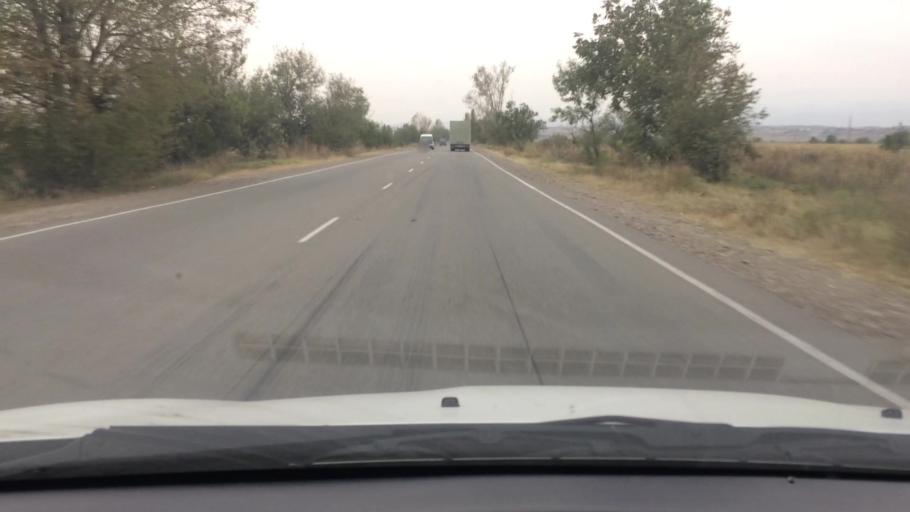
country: GE
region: Kvemo Kartli
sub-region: Marneuli
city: Marneuli
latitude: 41.5596
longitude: 44.7758
